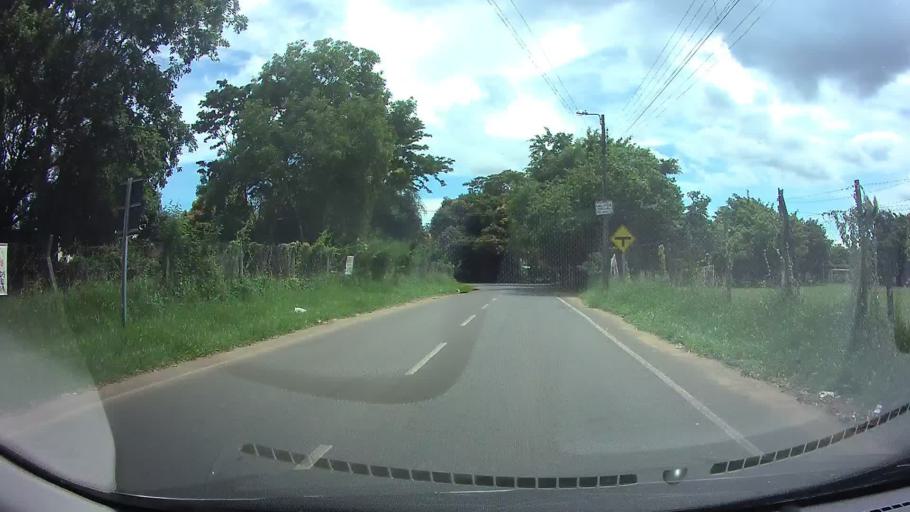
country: PY
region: Central
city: Fernando de la Mora
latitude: -25.3208
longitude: -57.5304
